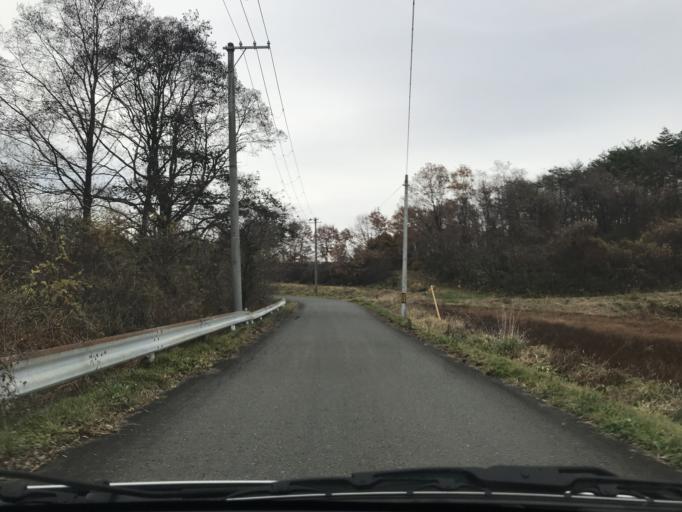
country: JP
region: Iwate
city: Ichinoseki
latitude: 38.9879
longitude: 141.0116
